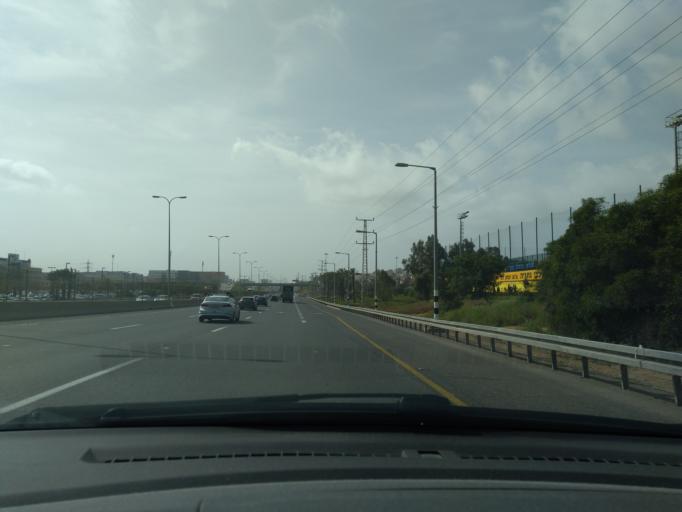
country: IL
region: Central District
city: Even Yehuda
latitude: 32.2920
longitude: 34.8608
